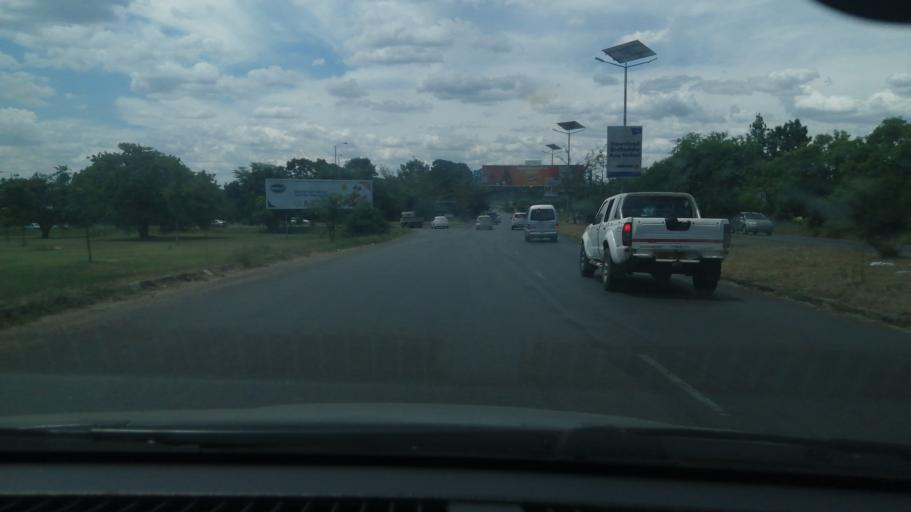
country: ZW
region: Harare
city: Harare
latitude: -17.8350
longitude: 31.1033
